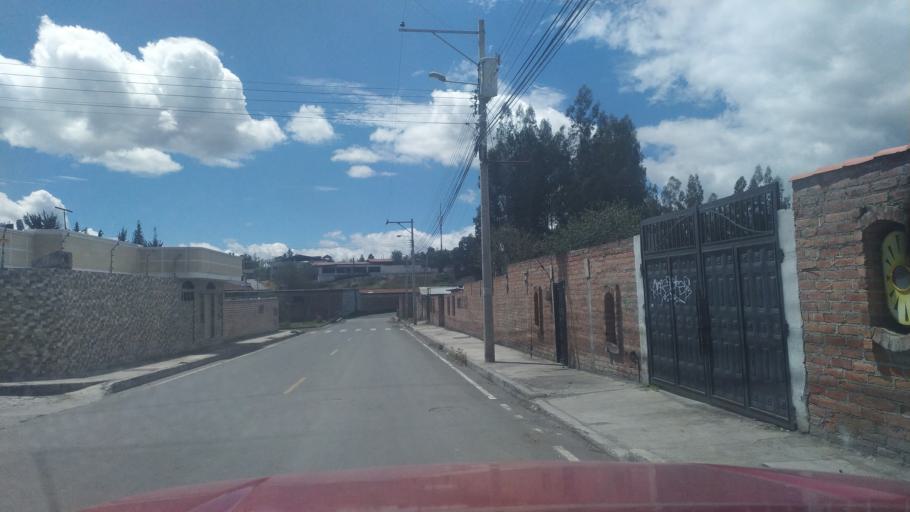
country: EC
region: Chimborazo
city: Riobamba
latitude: -1.6719
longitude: -78.6683
